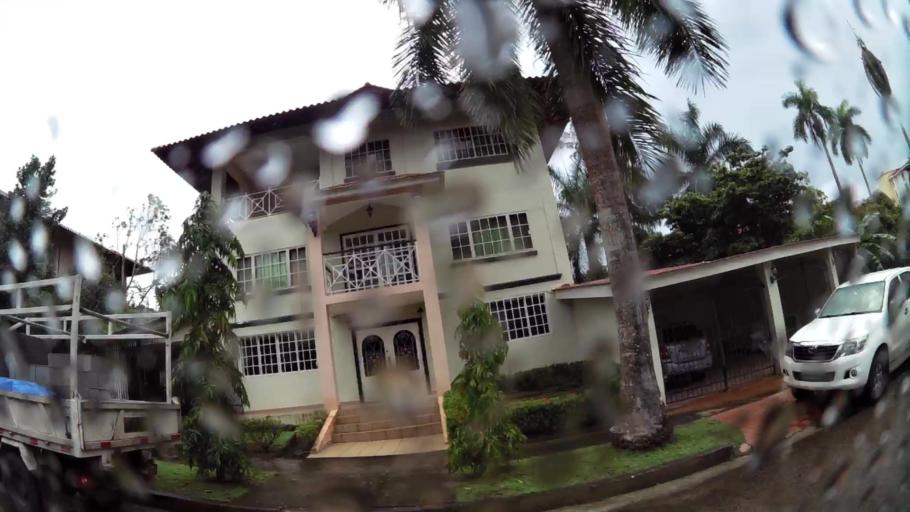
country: PA
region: Panama
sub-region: Distrito de Panama
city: Ancon
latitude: 8.9777
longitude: -79.5595
